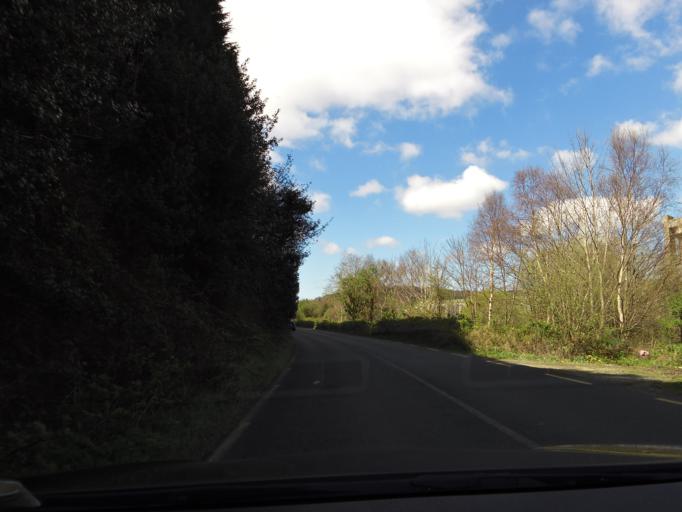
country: IE
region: Leinster
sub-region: Wicklow
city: Arklow
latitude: 52.8094
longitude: -6.1832
